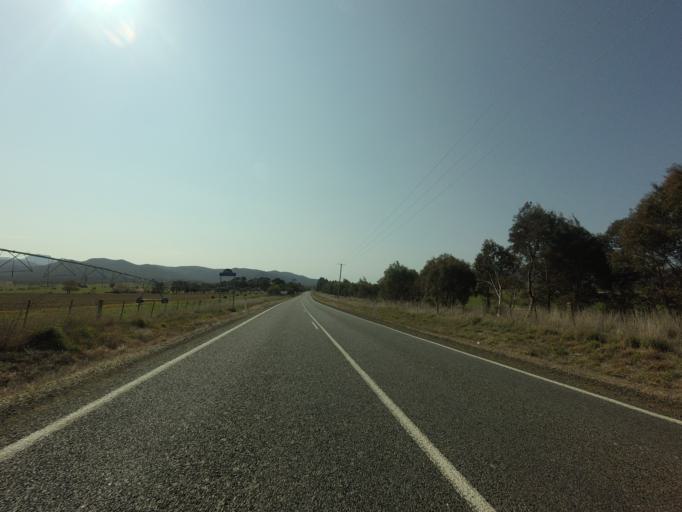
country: AU
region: Tasmania
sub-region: Northern Midlands
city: Evandale
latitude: -41.7897
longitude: 147.7127
